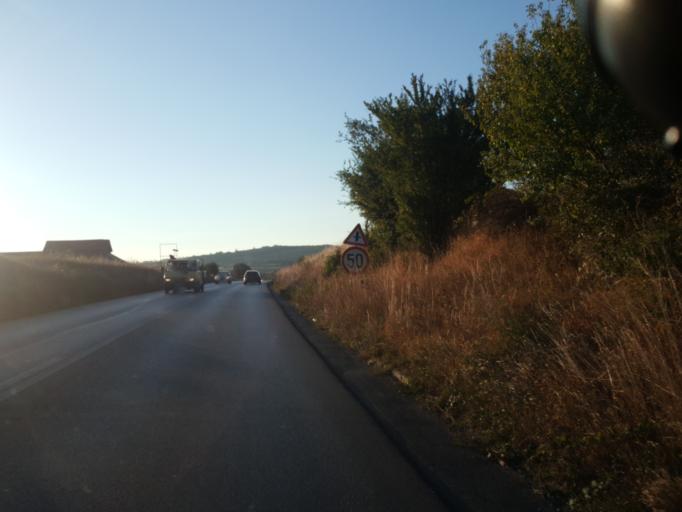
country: XK
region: Pec
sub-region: Komuna e Klines
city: Klina
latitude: 42.5927
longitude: 20.6617
